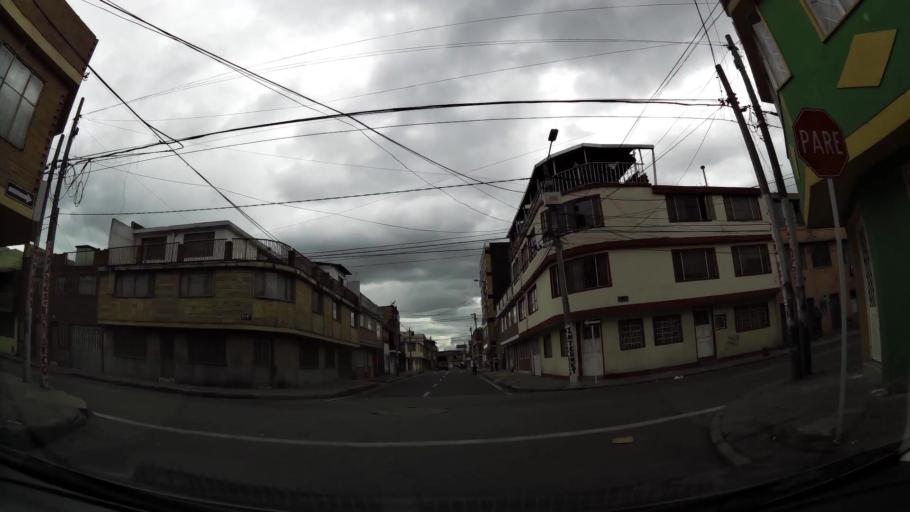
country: CO
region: Bogota D.C.
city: Barrio San Luis
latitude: 4.6988
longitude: -74.1031
